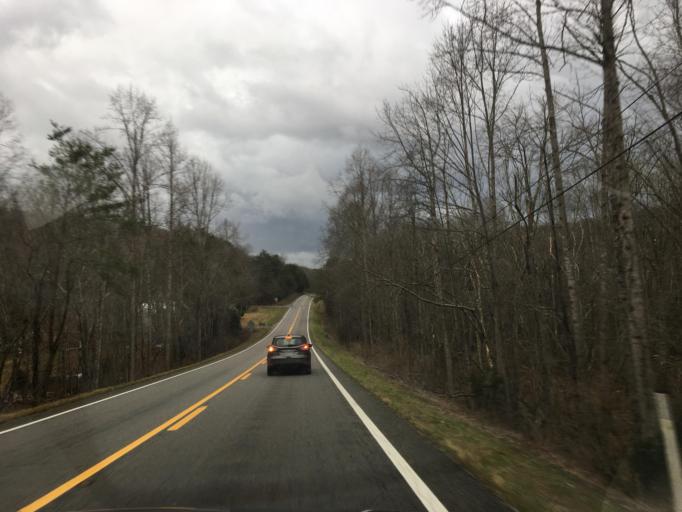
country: US
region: Tennessee
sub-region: Cumberland County
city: Crossville
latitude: 35.8770
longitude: -84.9341
